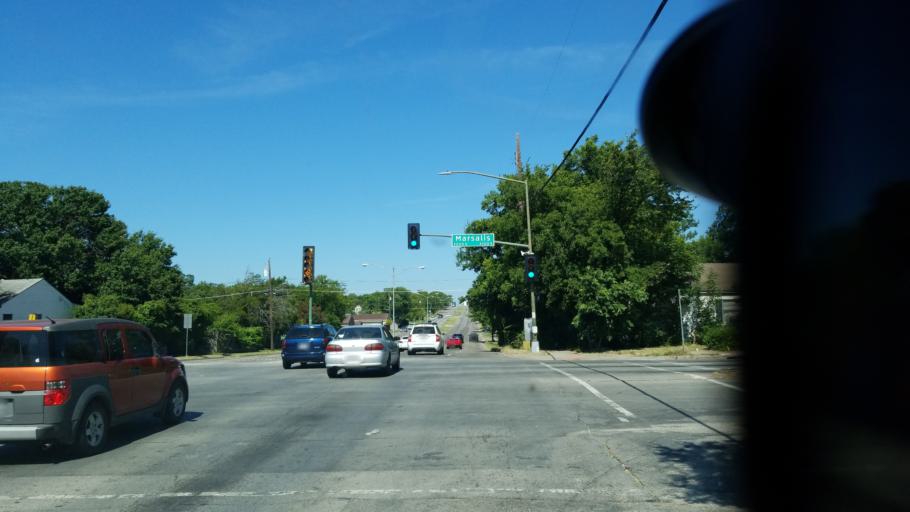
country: US
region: Texas
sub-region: Dallas County
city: Dallas
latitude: 32.7061
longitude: -96.8144
